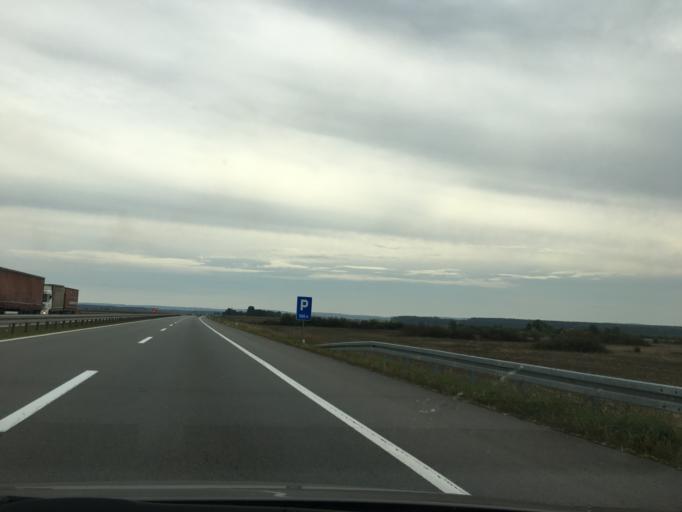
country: RS
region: Autonomna Pokrajina Vojvodina
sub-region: Juznobacki Okrug
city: Kovilj
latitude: 45.2247
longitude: 20.0566
